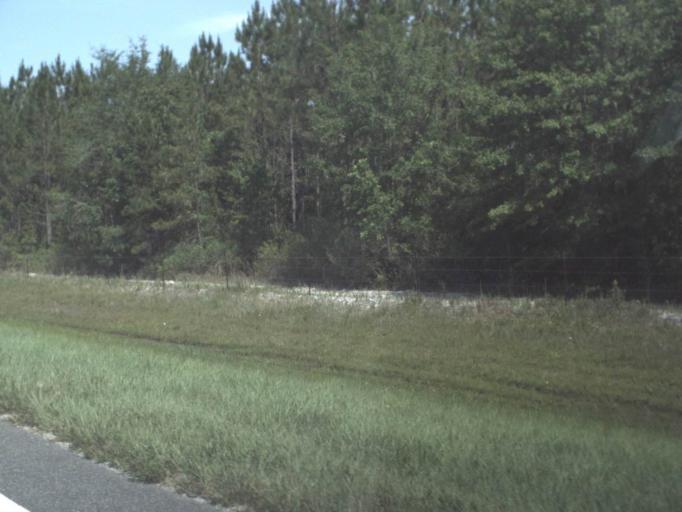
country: US
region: Florida
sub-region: Clay County
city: Asbury Lake
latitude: 29.9781
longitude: -81.8819
